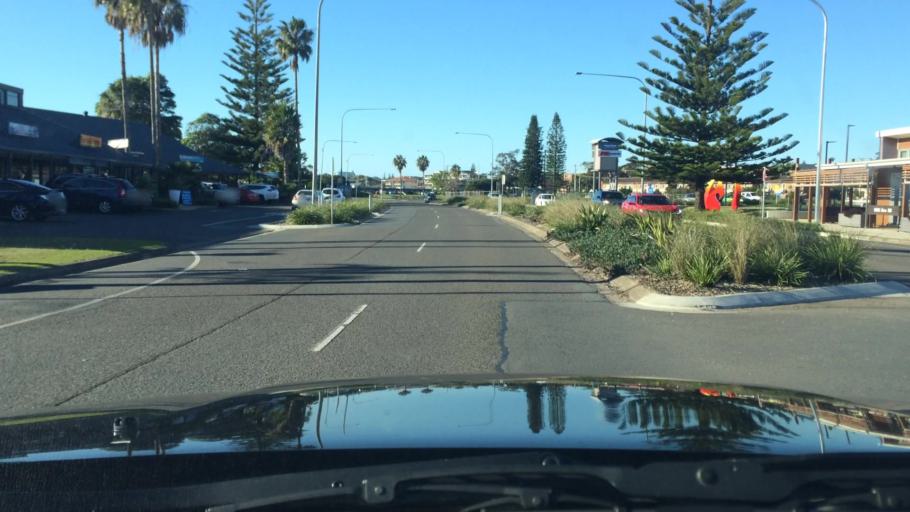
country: AU
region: New South Wales
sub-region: Port Macquarie-Hastings
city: Port Macquarie
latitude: -31.4282
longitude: 152.8979
